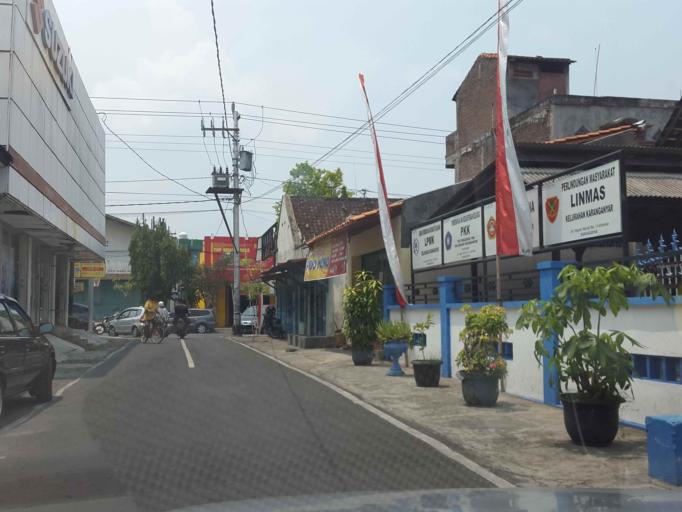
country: ID
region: Central Java
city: Jaten
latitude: -7.5962
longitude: 110.9490
